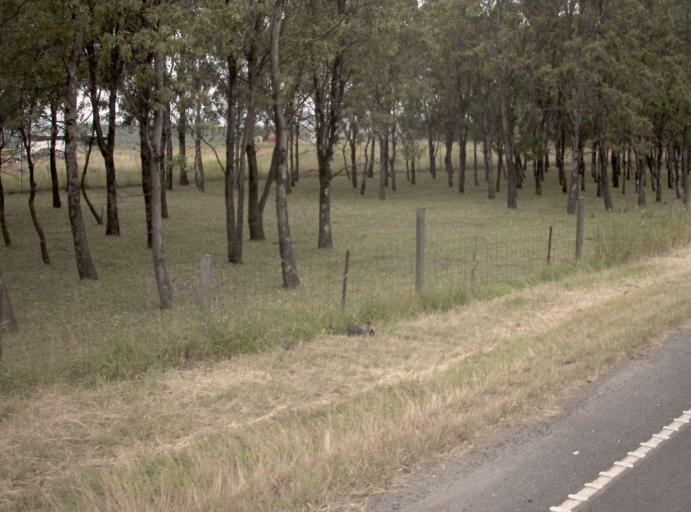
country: AU
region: Victoria
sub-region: Latrobe
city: Morwell
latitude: -38.2543
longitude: 146.4243
